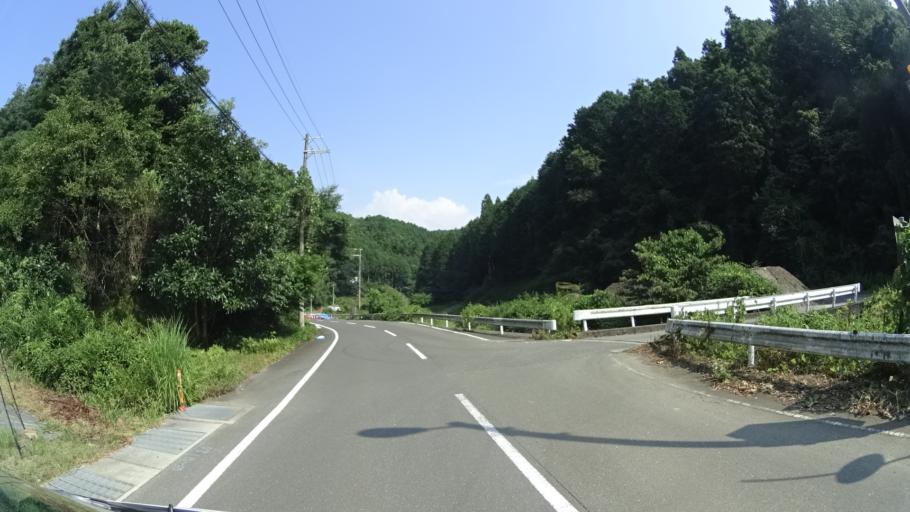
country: JP
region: Kyoto
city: Maizuru
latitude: 35.4203
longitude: 135.2236
